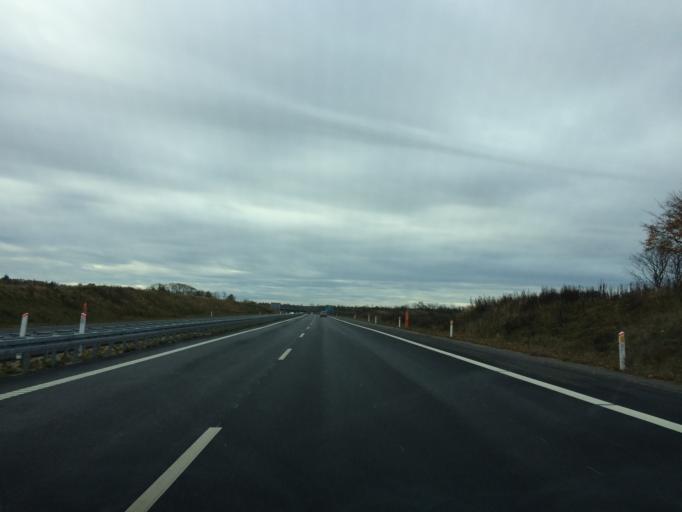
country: DK
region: Central Jutland
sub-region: Silkeborg Kommune
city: Silkeborg
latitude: 56.1971
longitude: 9.5054
